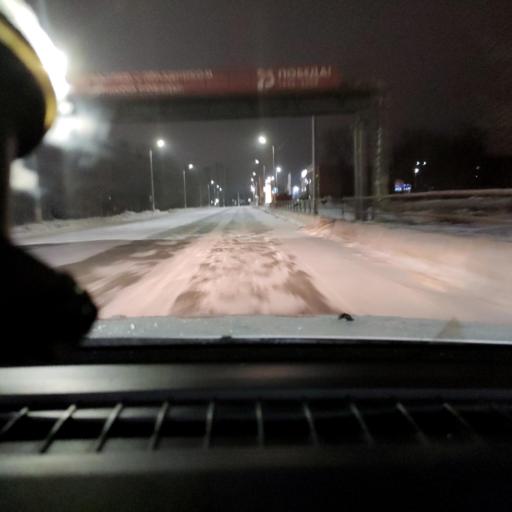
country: RU
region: Samara
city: Novokuybyshevsk
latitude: 53.0884
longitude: 49.9450
